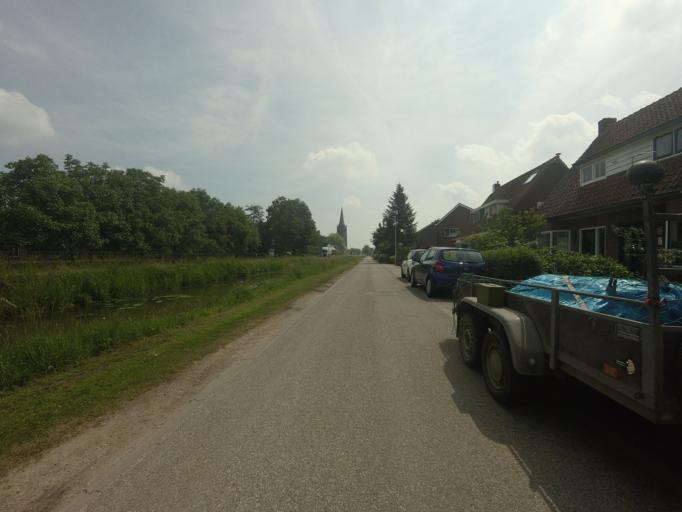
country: NL
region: Utrecht
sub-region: Gemeente Houten
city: Houten
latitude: 51.9957
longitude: 5.1797
